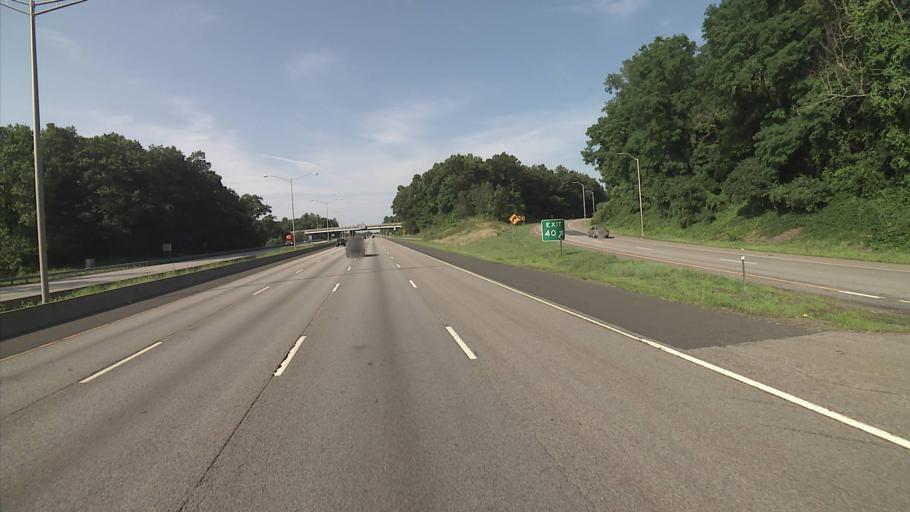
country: US
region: Connecticut
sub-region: Hartford County
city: Windsor Locks
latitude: 41.9016
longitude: -72.6372
